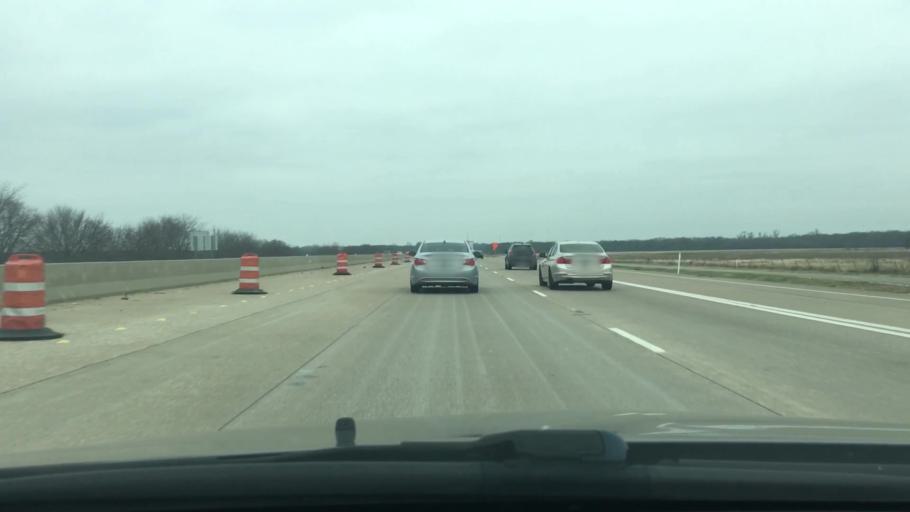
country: US
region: Texas
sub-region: Navarro County
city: Corsicana
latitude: 32.1759
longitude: -96.4709
